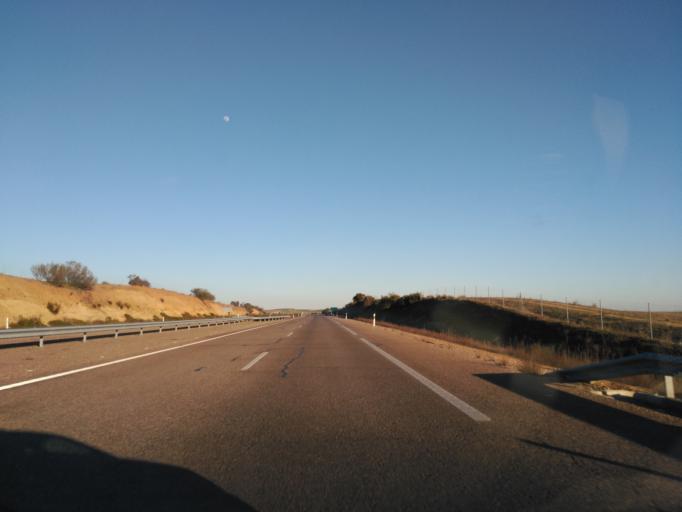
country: ES
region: Castille and Leon
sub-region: Provincia de Zamora
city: Canizal
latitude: 41.1659
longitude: -5.3992
